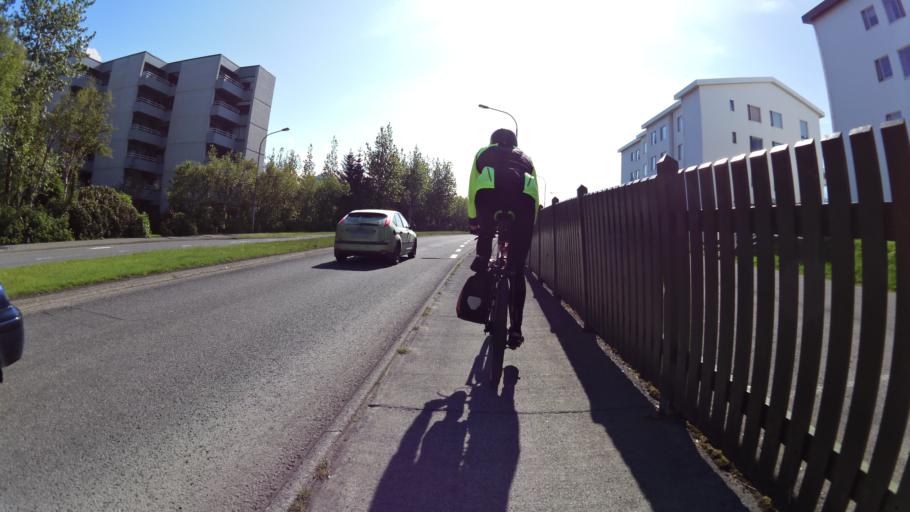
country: IS
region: Capital Region
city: Reykjavik
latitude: 64.1280
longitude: -21.8940
